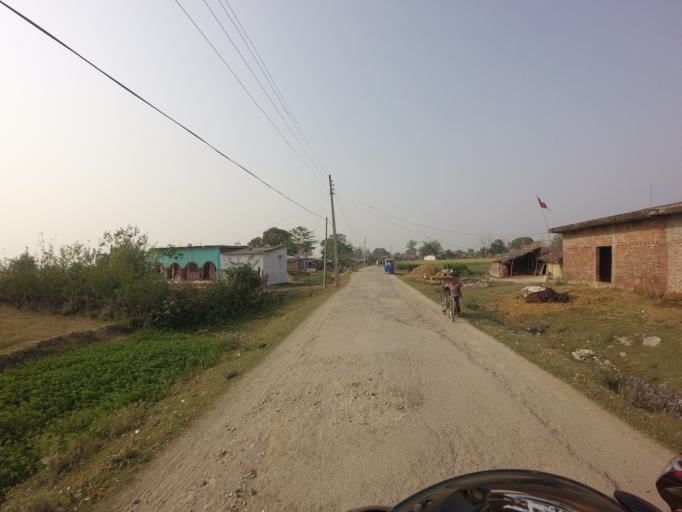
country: NP
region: Mid Western
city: Gulariya
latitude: 28.1939
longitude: 81.3382
